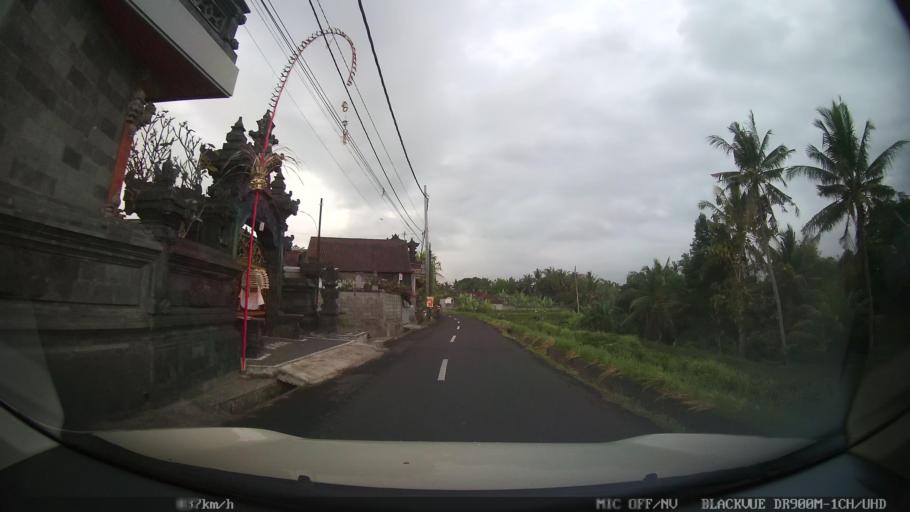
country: ID
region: Bali
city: Banjar Pasekan
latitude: -8.6121
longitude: 115.2926
